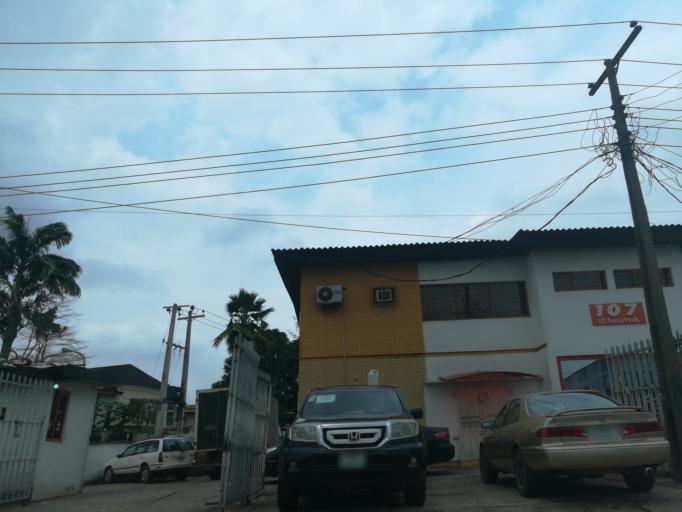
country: NG
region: Lagos
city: Agege
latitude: 6.6187
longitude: 3.3457
